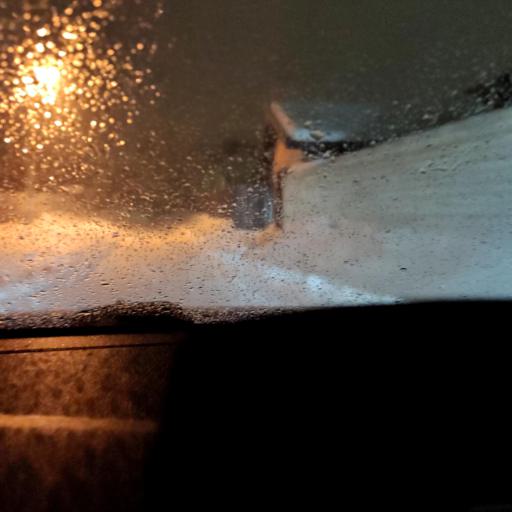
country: RU
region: Tatarstan
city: Stolbishchi
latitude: 55.7483
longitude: 49.2958
